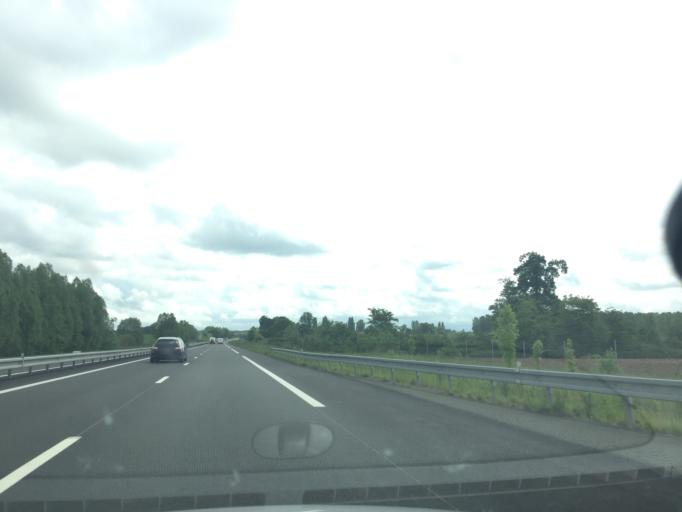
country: FR
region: Pays de la Loire
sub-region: Departement de la Sarthe
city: Brette-les-Pins
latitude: 47.8977
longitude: 0.3048
